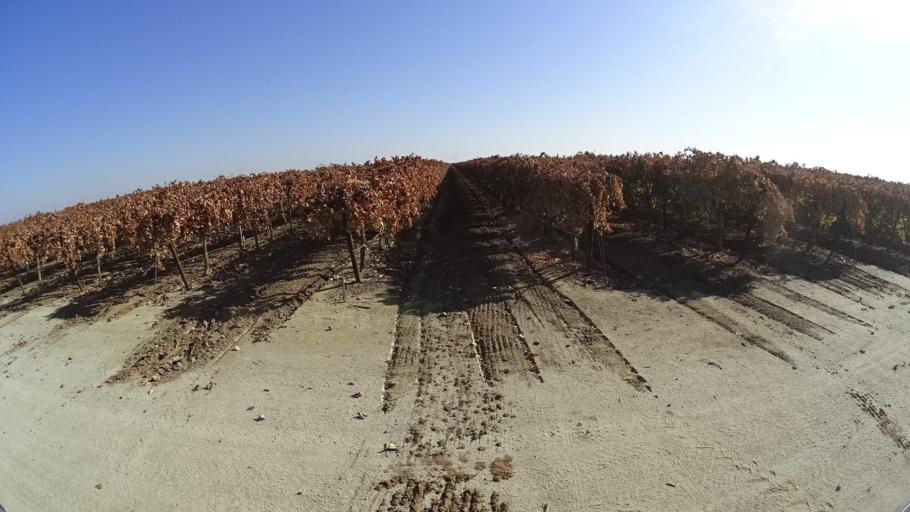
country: US
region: California
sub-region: Kern County
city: Delano
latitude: 35.7430
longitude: -119.2142
